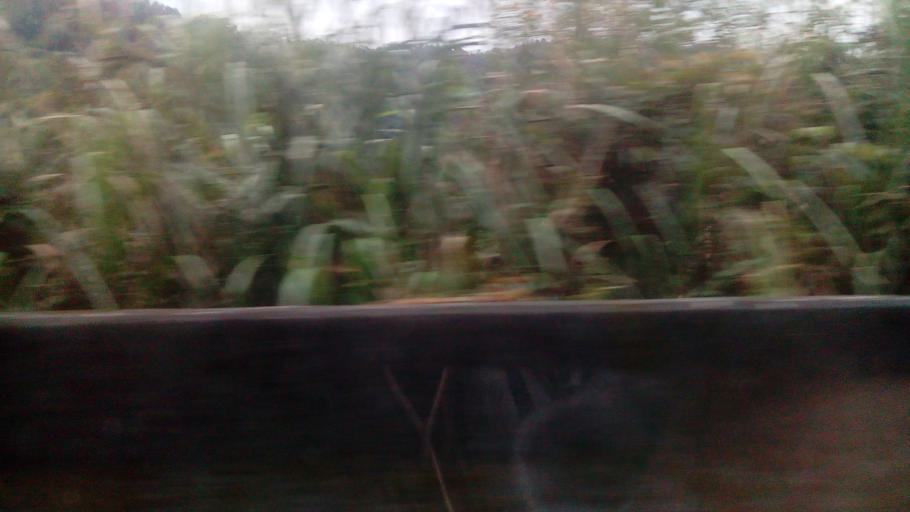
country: TW
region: Taiwan
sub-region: Yilan
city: Yilan
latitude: 24.6344
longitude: 121.5521
